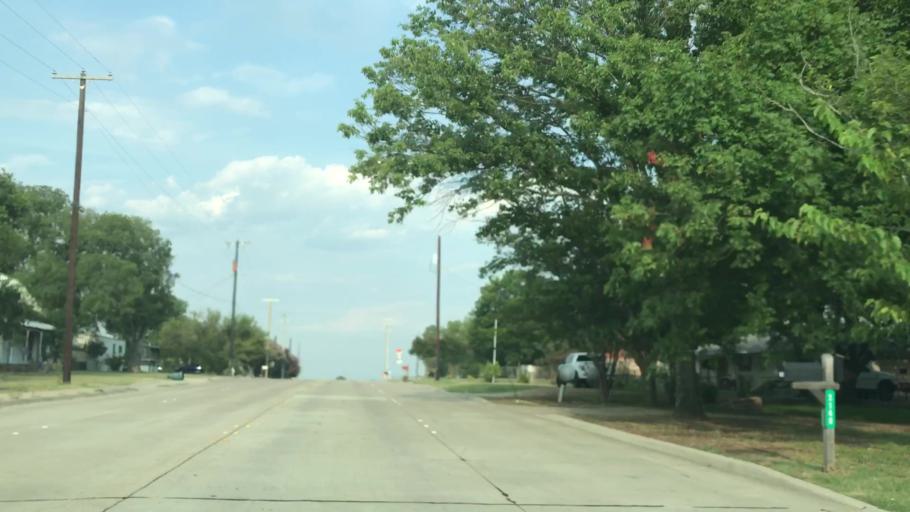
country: US
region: Texas
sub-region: Rockwall County
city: Rockwall
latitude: 32.9251
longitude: -96.4207
